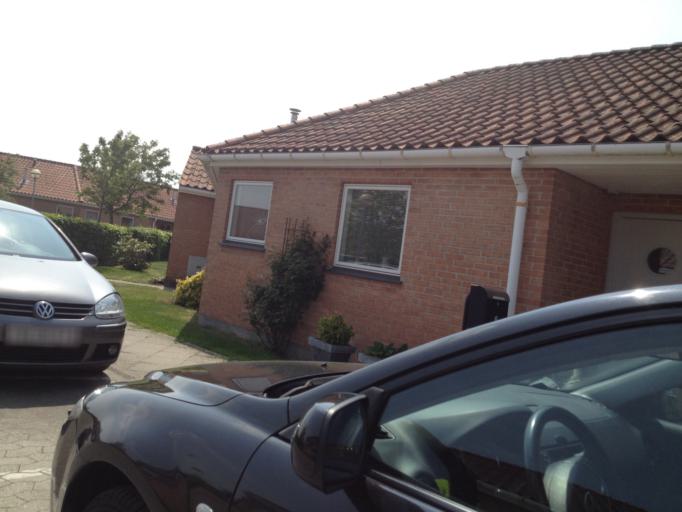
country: DK
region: Capital Region
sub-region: Ballerup Kommune
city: Malov
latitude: 55.7490
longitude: 12.3425
